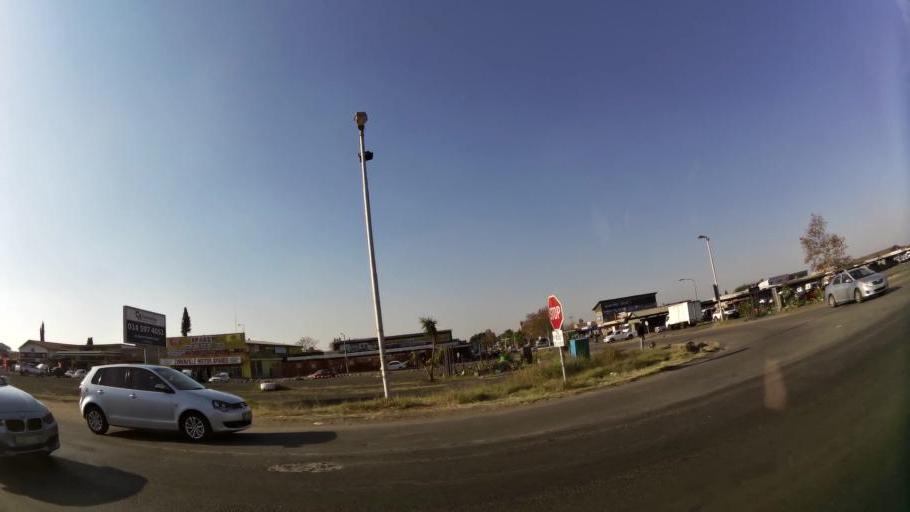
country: ZA
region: North-West
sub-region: Bojanala Platinum District Municipality
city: Rustenburg
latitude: -25.6499
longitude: 27.2382
